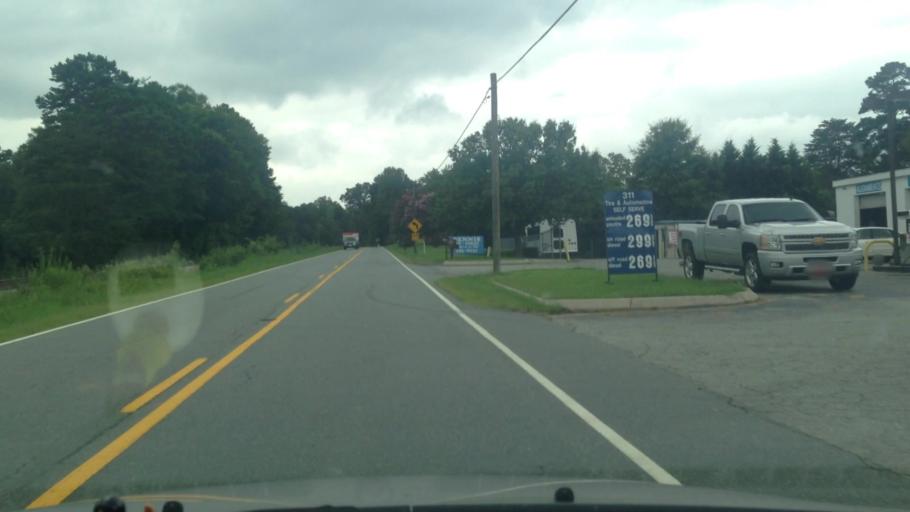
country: US
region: North Carolina
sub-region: Forsyth County
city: Walkertown
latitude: 36.2284
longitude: -80.1673
